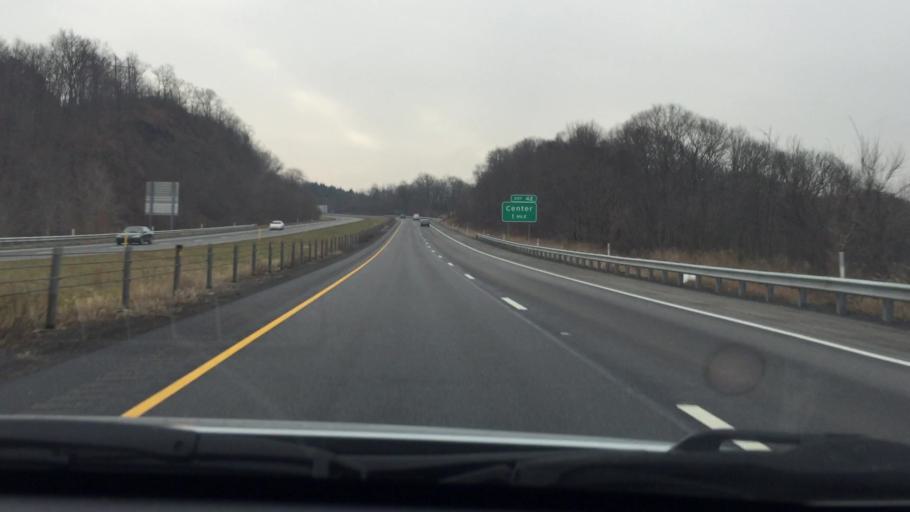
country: US
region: Pennsylvania
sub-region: Beaver County
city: Beaver
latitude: 40.6556
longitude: -80.3246
